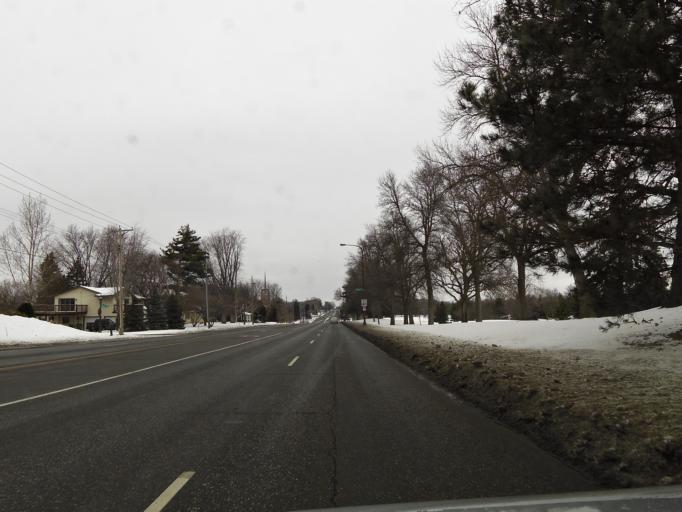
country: US
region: Minnesota
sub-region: Ramsey County
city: Little Canada
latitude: 44.9887
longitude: -93.0659
